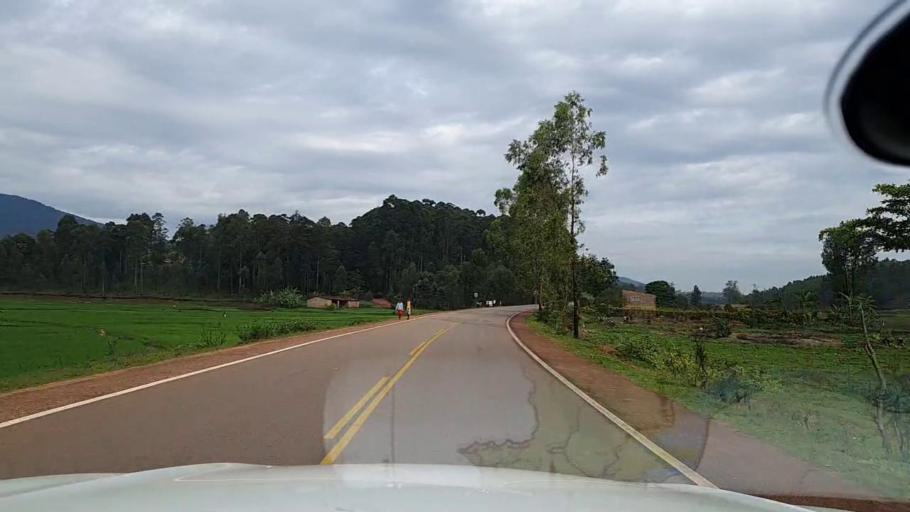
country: RW
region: Southern Province
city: Butare
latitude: -2.5653
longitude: 29.7248
